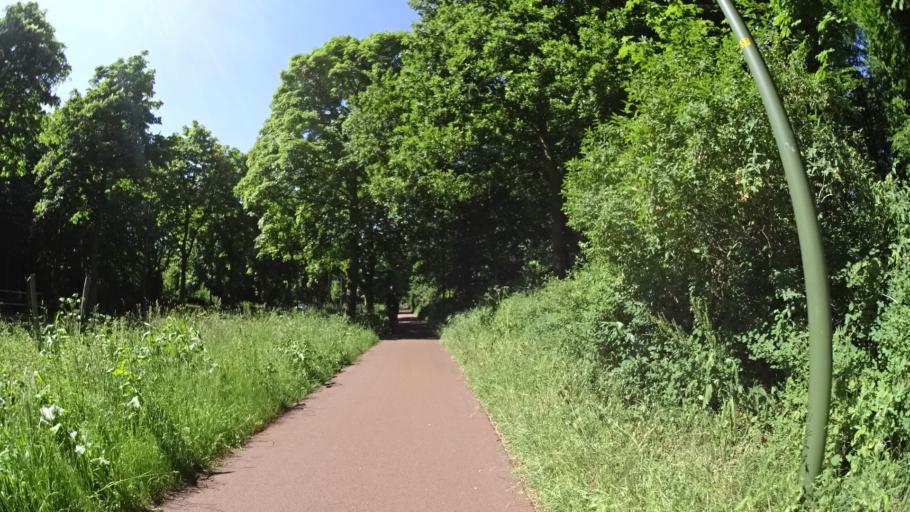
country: NL
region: South Holland
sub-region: Gemeente Den Haag
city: Scheveningen
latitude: 52.0934
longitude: 4.2896
